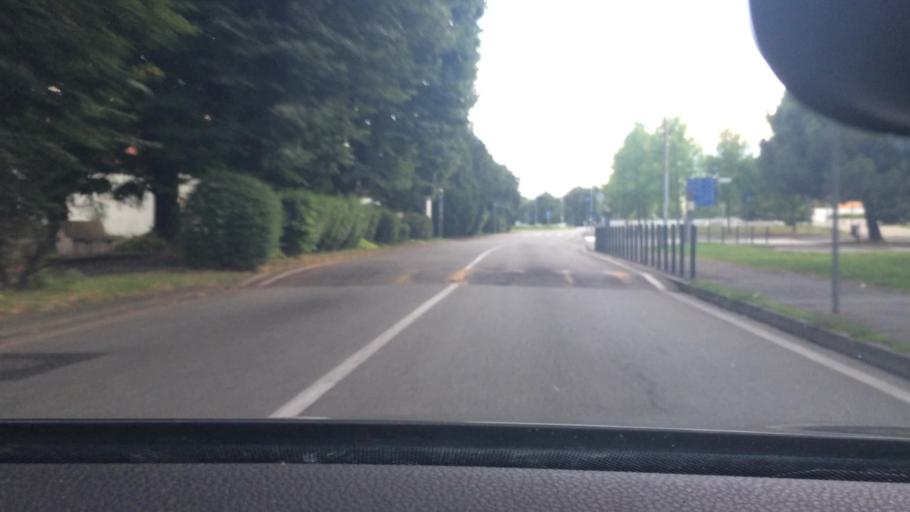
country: IT
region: Lombardy
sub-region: Citta metropolitana di Milano
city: Vanzago
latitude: 45.5243
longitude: 8.9903
